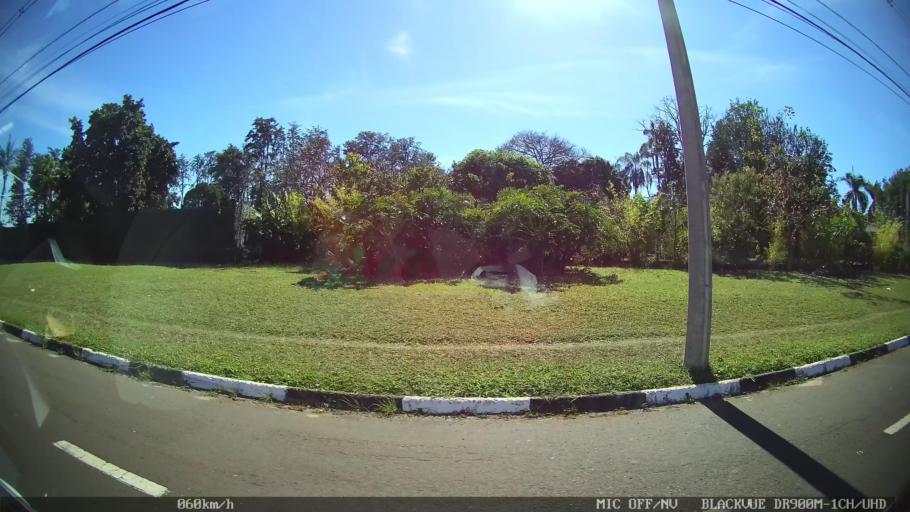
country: BR
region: Sao Paulo
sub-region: Franca
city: Franca
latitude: -20.5640
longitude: -47.3621
